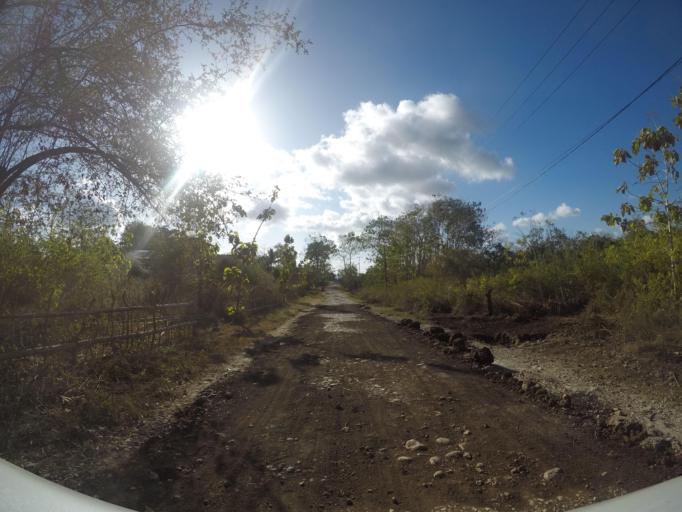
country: TL
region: Lautem
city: Lospalos
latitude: -8.4427
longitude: 126.8644
